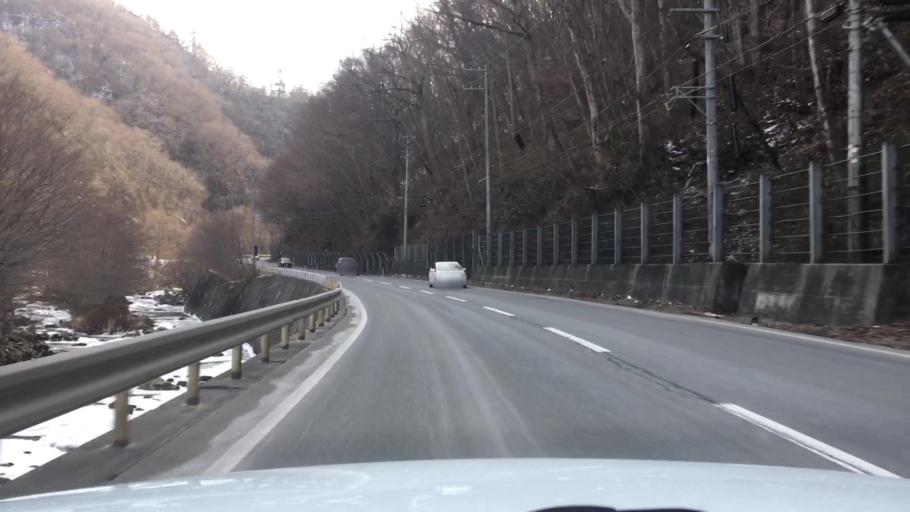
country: JP
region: Iwate
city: Tono
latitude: 39.6381
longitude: 141.5365
